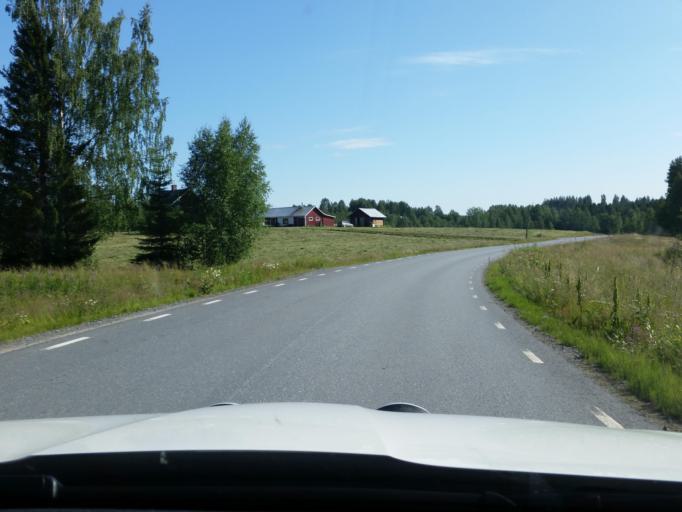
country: SE
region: Norrbotten
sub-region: Alvsbyns Kommun
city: AElvsbyn
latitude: 65.6627
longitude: 20.8790
